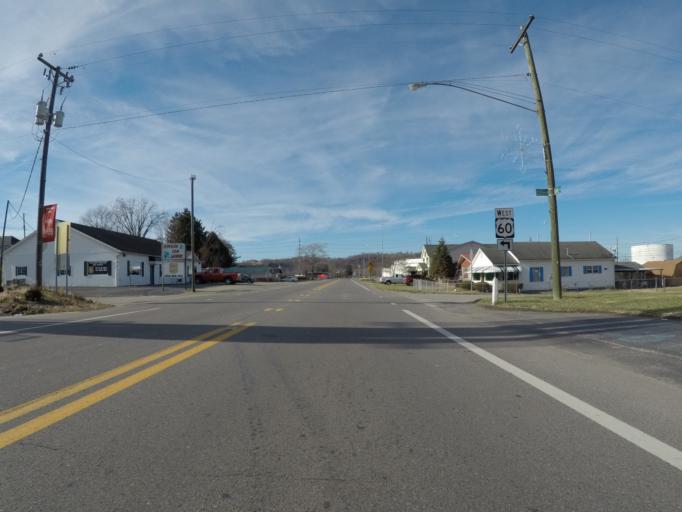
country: US
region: West Virginia
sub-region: Wayne County
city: Kenova
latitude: 38.4036
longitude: -82.5855
